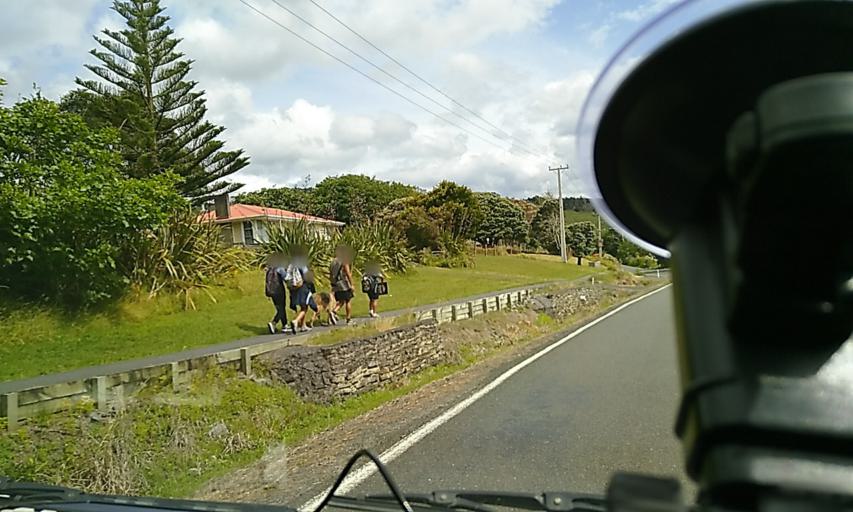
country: NZ
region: Northland
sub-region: Far North District
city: Ahipara
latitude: -35.5253
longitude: 173.3900
